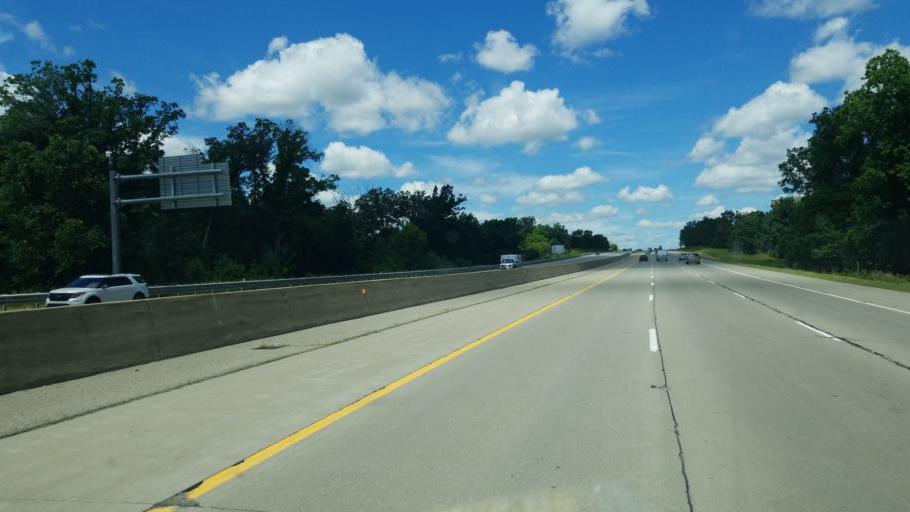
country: US
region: Michigan
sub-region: Livingston County
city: Brighton
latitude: 42.5541
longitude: -83.8162
